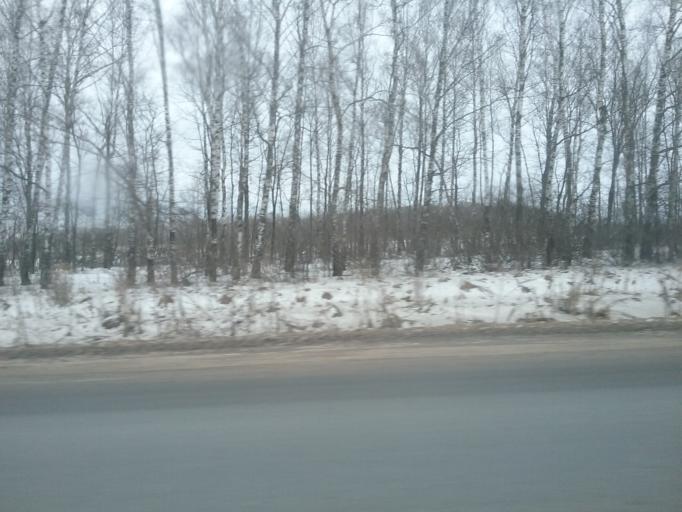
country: RU
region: Tula
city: Skuratovskiy
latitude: 54.1248
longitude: 37.6882
